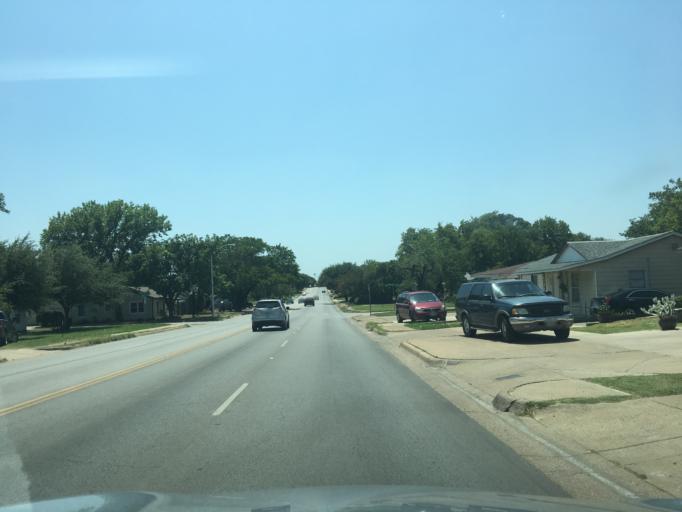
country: US
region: Texas
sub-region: Tarrant County
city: Edgecliff Village
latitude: 32.6807
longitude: -97.3530
